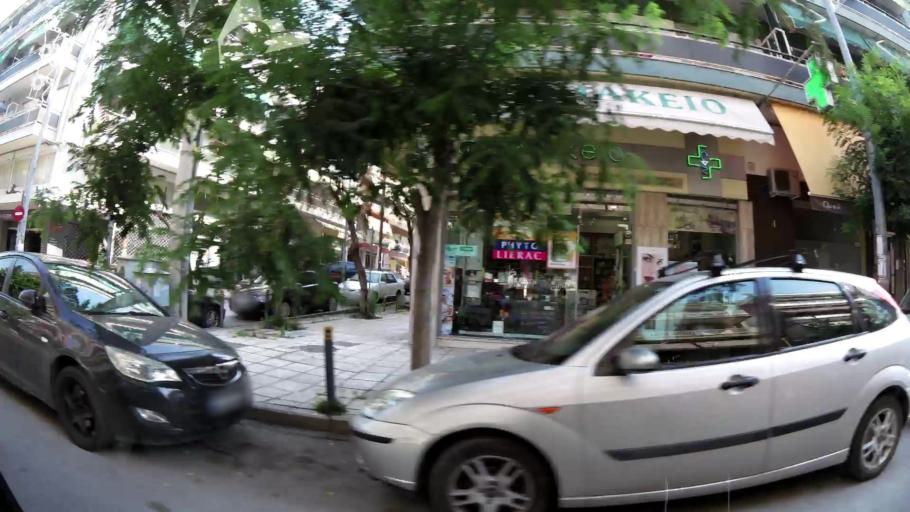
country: GR
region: Central Macedonia
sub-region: Nomos Thessalonikis
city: Sykies
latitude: 40.6524
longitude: 22.9501
